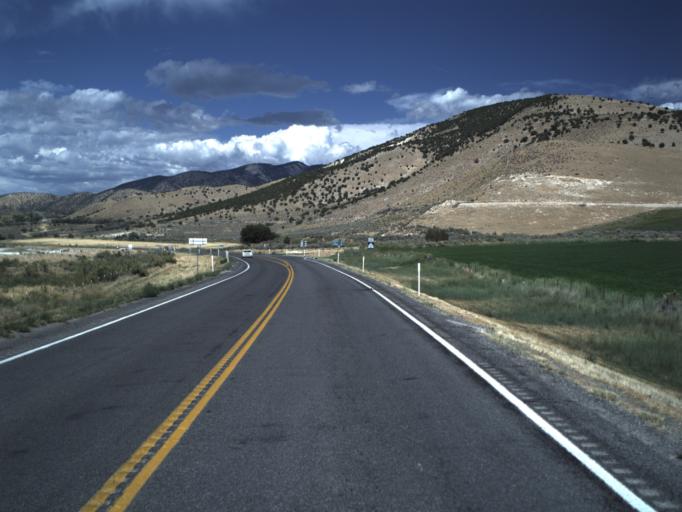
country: US
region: Utah
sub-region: Sanpete County
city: Gunnison
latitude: 39.1703
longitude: -111.7080
